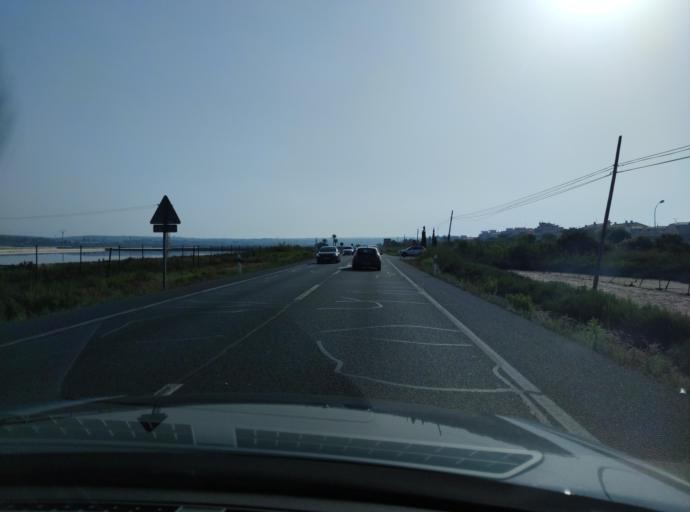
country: ES
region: Valencia
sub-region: Provincia de Alicante
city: Santa Pola
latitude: 38.1923
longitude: -0.5924
